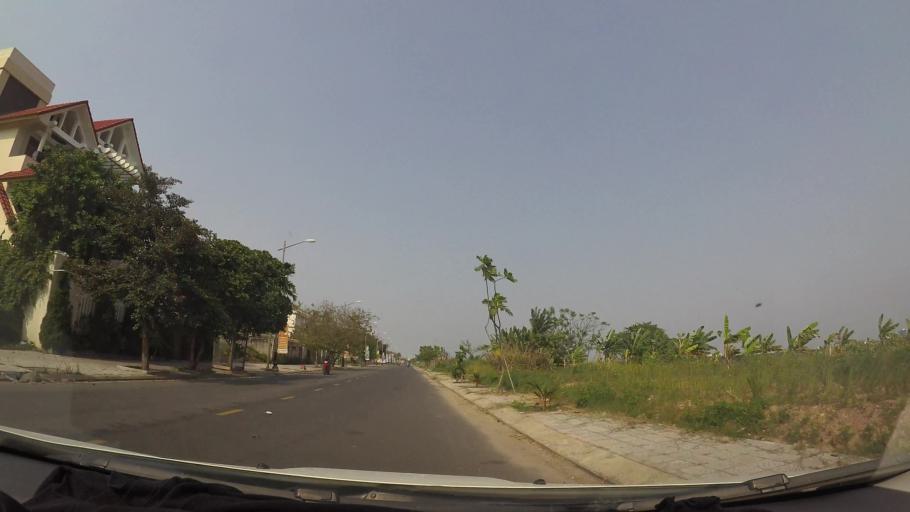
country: VN
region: Da Nang
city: Cam Le
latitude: 16.0042
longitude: 108.1972
